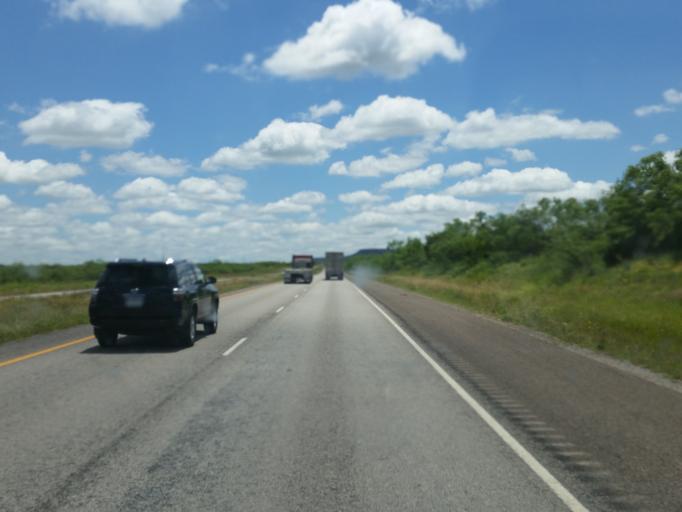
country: US
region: Texas
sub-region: Scurry County
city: Snyder
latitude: 32.9823
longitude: -101.1166
